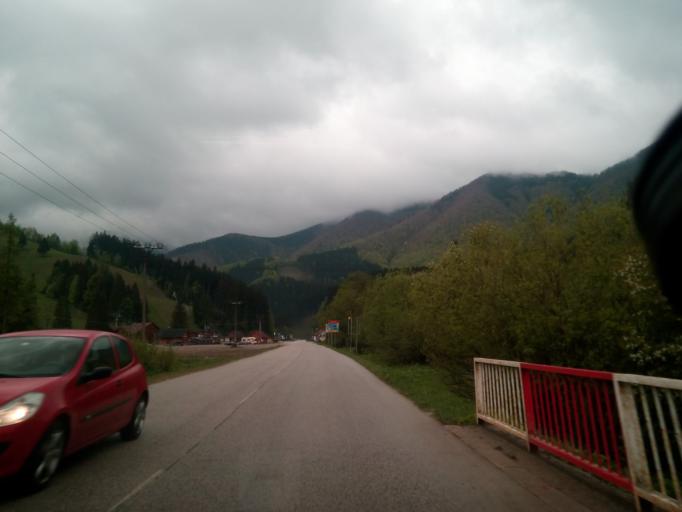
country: SK
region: Zilinsky
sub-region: Okres Zilina
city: Terchova
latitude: 49.2314
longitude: 19.0372
